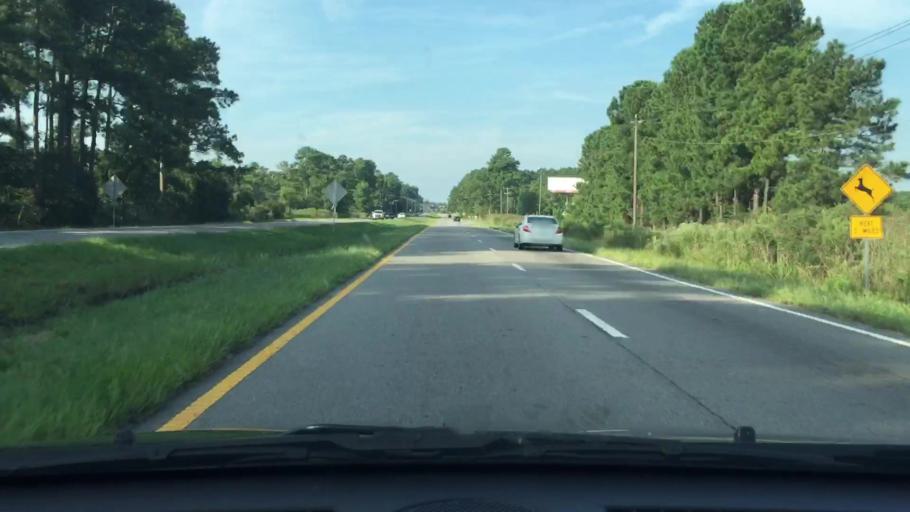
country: US
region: Virginia
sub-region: Isle of Wight County
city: Carrollton
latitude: 36.9634
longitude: -76.5173
